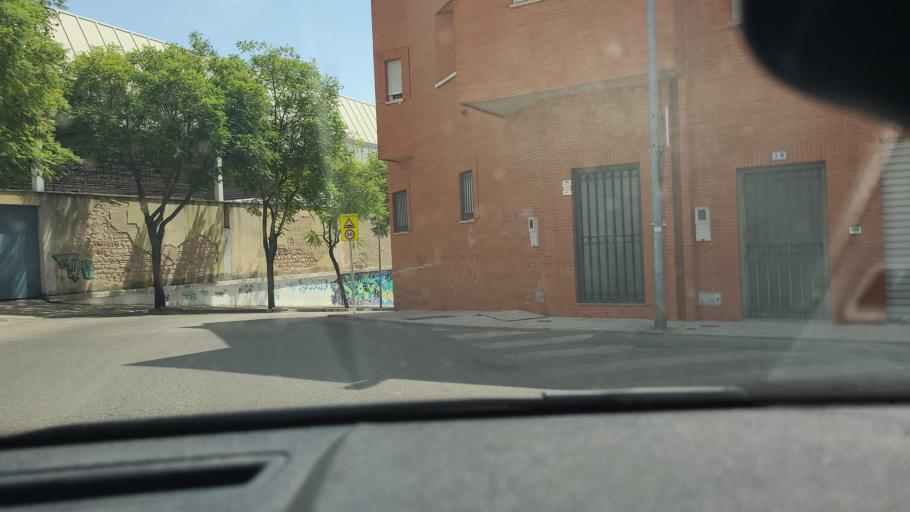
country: ES
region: Andalusia
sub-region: Provincia de Jaen
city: Linares
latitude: 38.0968
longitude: -3.6280
